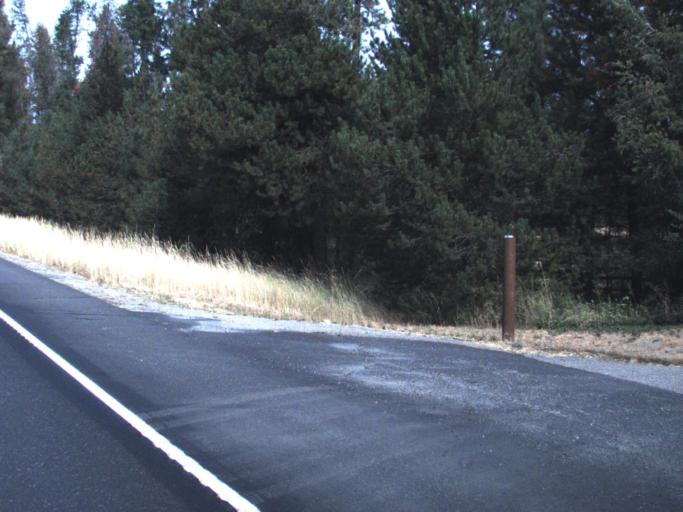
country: US
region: Washington
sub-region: Spokane County
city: Deer Park
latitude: 47.8935
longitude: -117.4300
